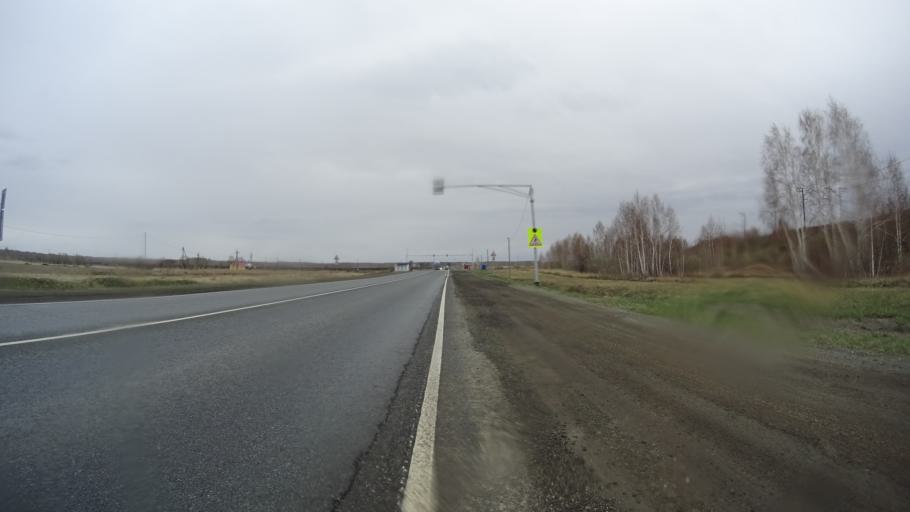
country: RU
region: Chelyabinsk
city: Krasnogorskiy
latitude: 54.6237
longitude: 61.2804
